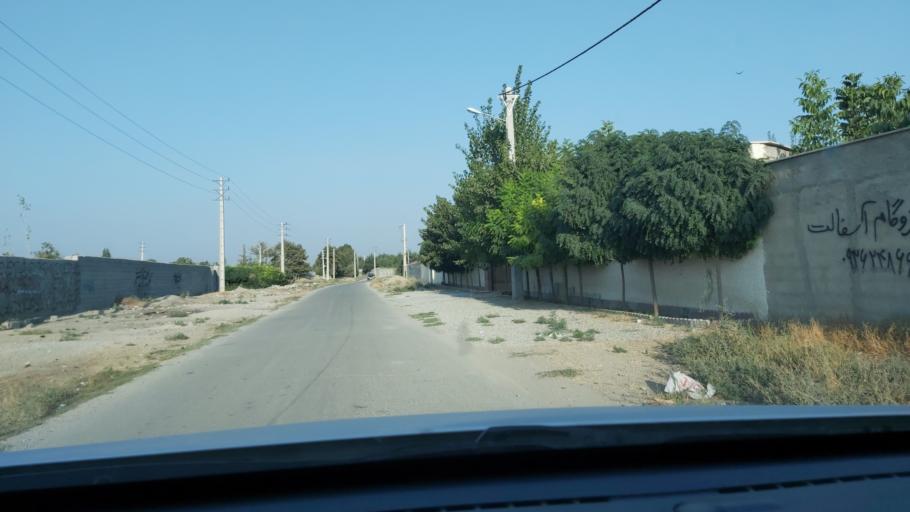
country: IR
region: Alborz
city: Hashtgerd
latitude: 35.8591
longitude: 50.6987
